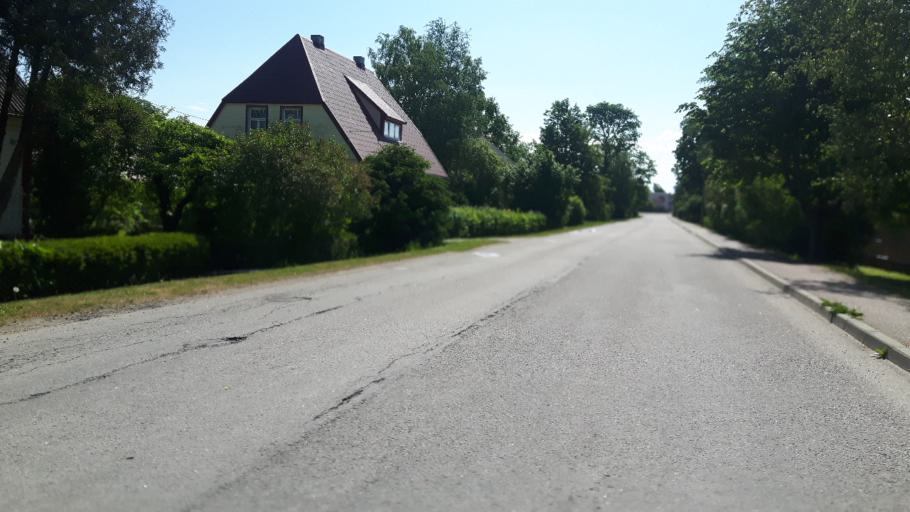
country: EE
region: Paernumaa
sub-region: Vaendra vald (alev)
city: Vandra
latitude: 58.6506
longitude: 25.0274
